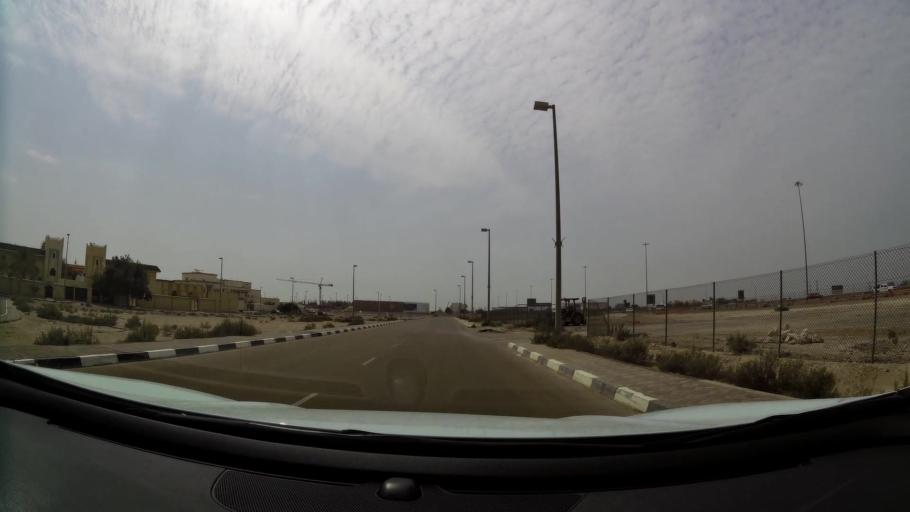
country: AE
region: Abu Dhabi
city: Abu Dhabi
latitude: 24.5387
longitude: 54.6864
